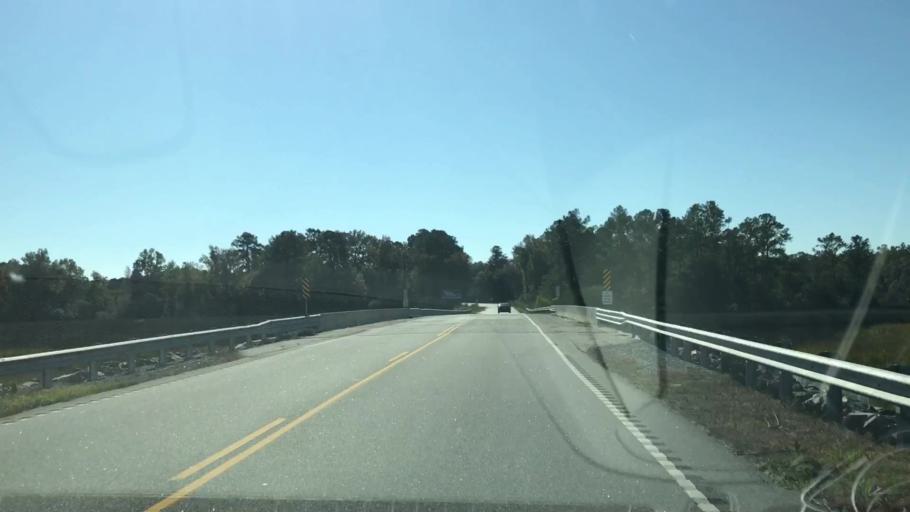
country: US
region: South Carolina
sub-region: Jasper County
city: Ridgeland
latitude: 32.5438
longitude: -80.9124
